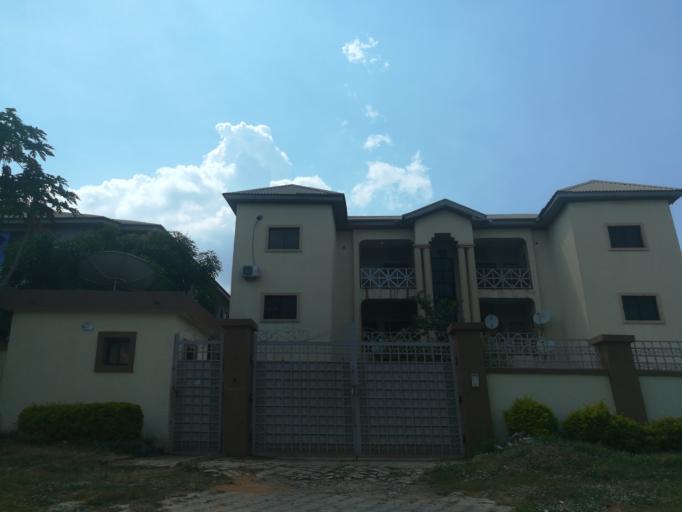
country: NG
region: Abuja Federal Capital Territory
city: Abuja
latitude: 9.0488
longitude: 7.4465
